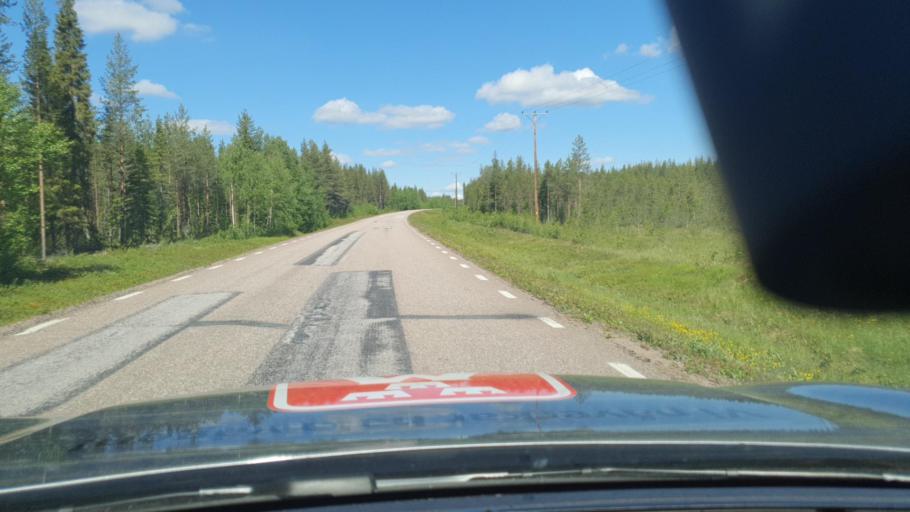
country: SE
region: Norrbotten
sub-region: Overkalix Kommun
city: OEverkalix
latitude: 67.0116
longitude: 22.5322
